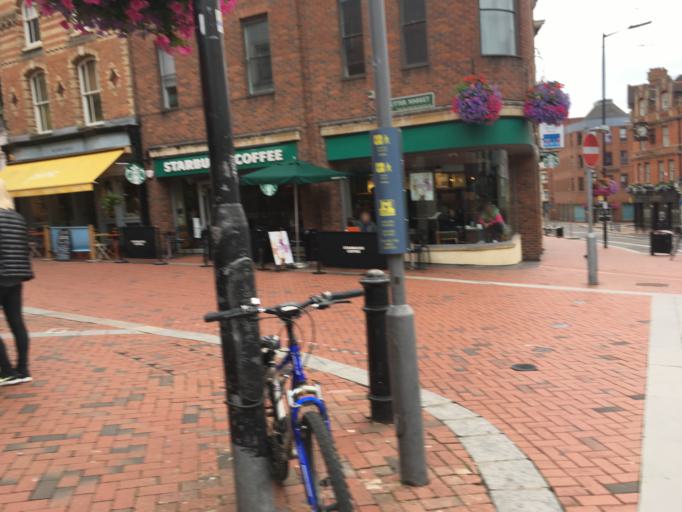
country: GB
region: England
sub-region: Reading
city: Reading
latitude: 51.4552
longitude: -0.9702
